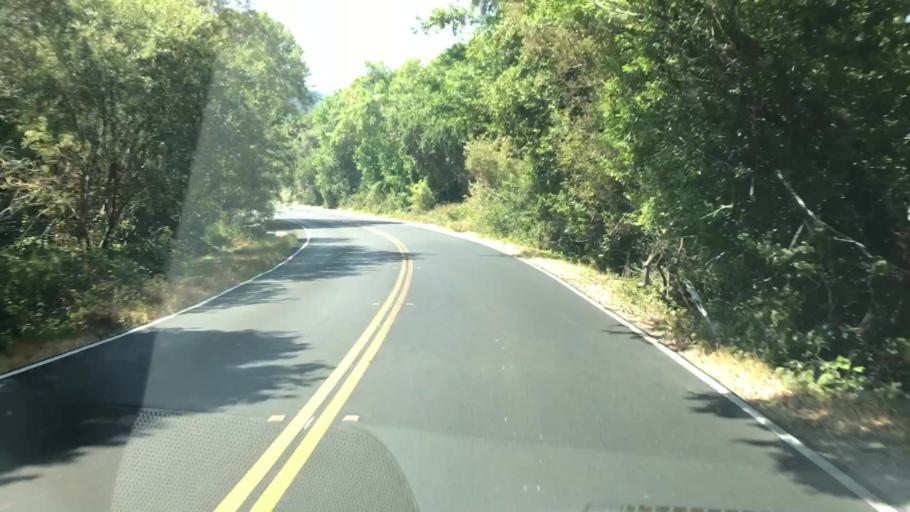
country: US
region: California
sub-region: Marin County
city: Bolinas
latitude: 37.9467
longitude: -122.7086
